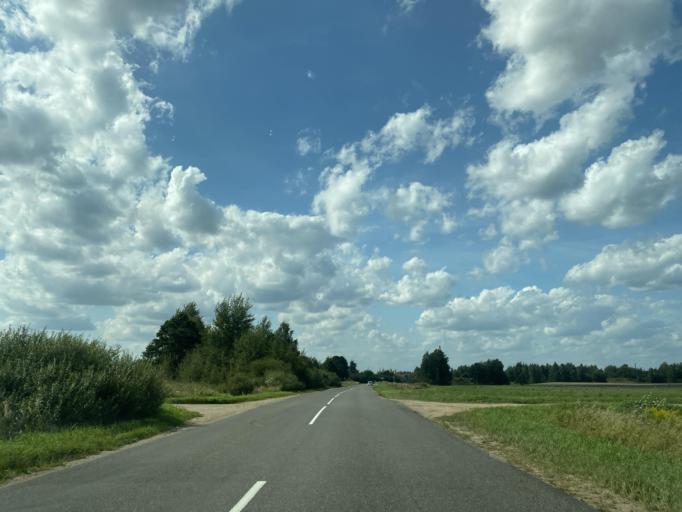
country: BY
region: Minsk
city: Horad Zhodzina
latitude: 54.0781
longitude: 28.3872
